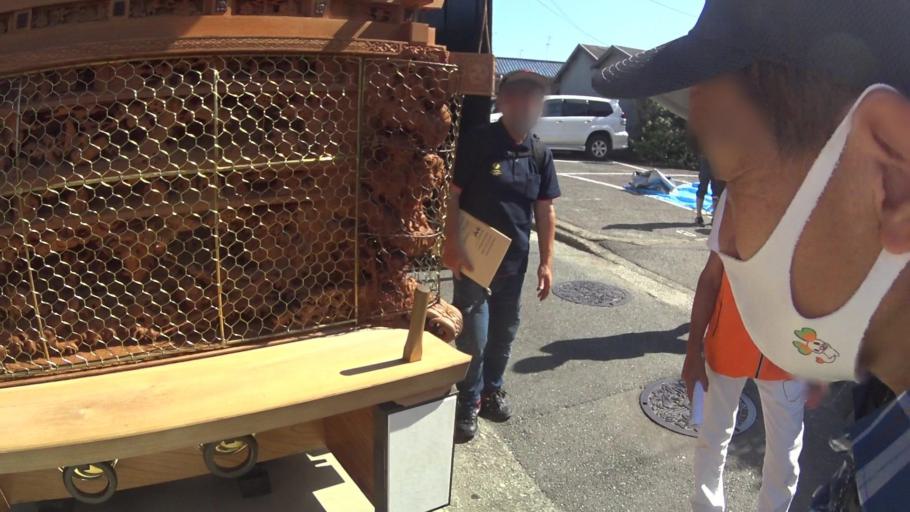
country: JP
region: Osaka
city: Takaishi
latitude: 34.5369
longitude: 135.4735
